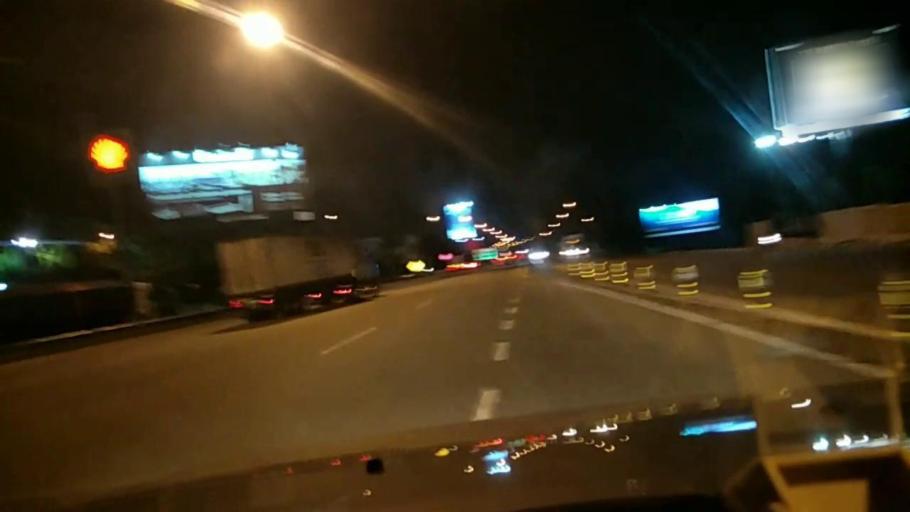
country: MY
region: Penang
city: Juru
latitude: 5.3253
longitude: 100.4365
